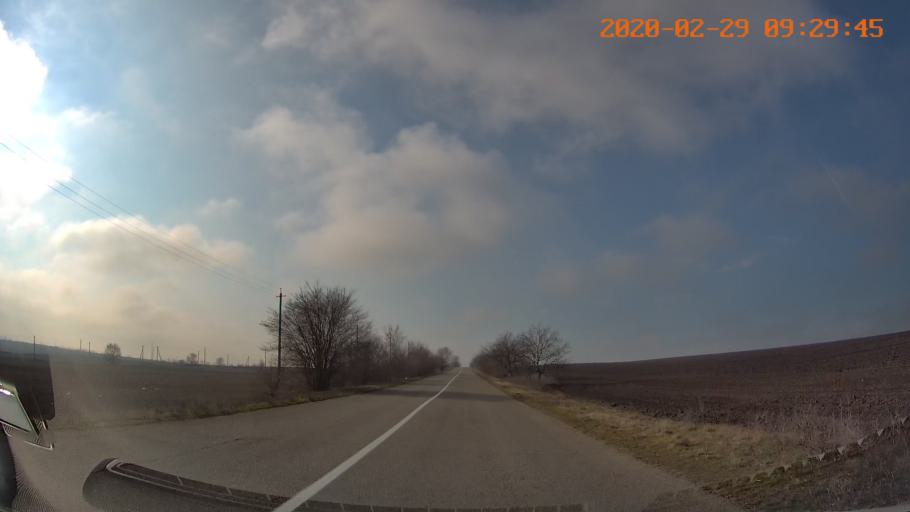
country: UA
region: Odessa
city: Lymanske
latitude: 46.6748
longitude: 29.9197
